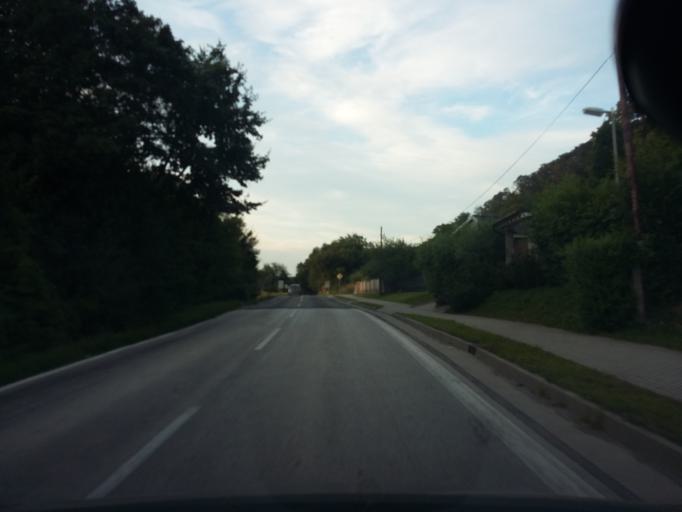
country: SK
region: Bratislavsky
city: Svaty Jur
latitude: 48.3706
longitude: 17.1468
